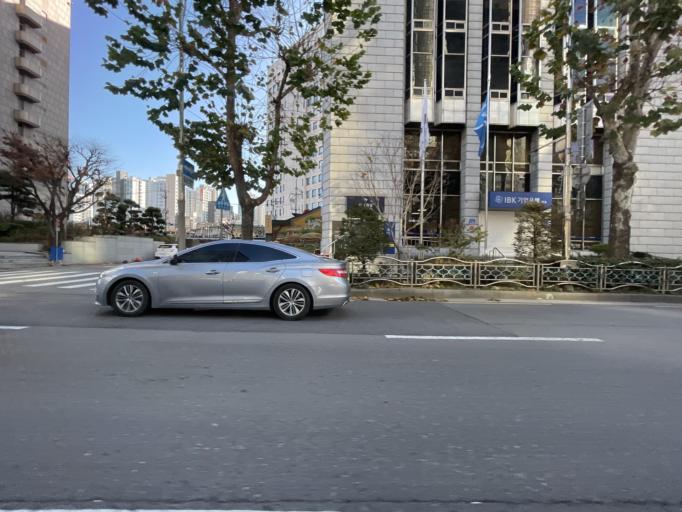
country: KR
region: Seoul
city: Seoul
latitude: 37.5450
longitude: 126.9519
